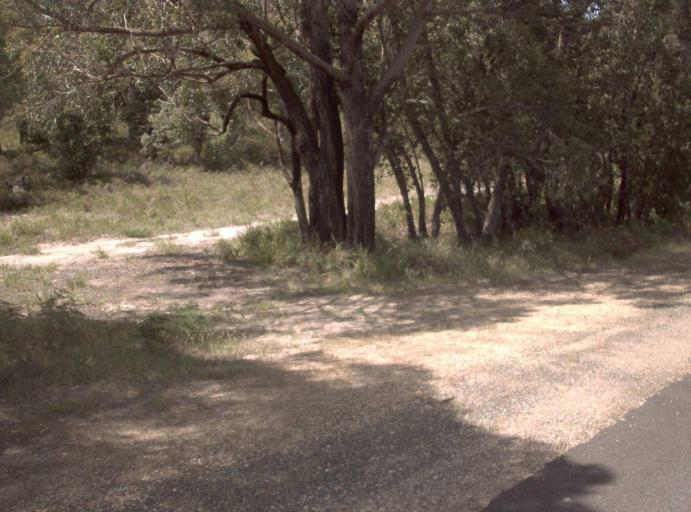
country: AU
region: Victoria
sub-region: Wellington
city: Sale
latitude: -37.9172
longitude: 147.2904
